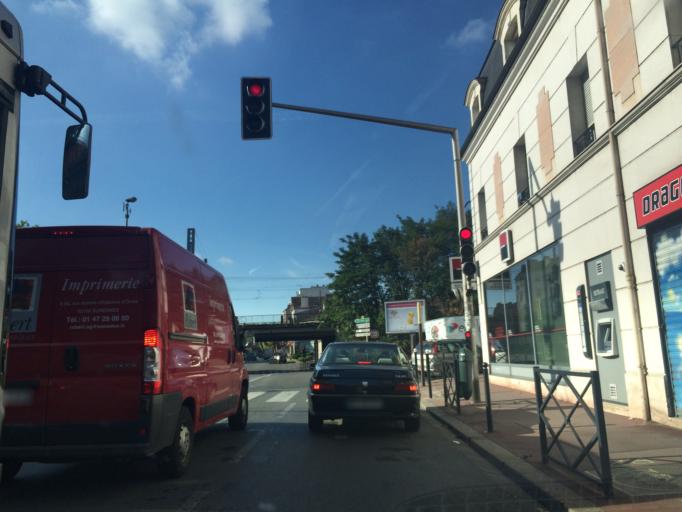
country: FR
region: Ile-de-France
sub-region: Departement du Val-de-Marne
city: Champigny-sur-Marne
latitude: 48.8081
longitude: 2.5092
